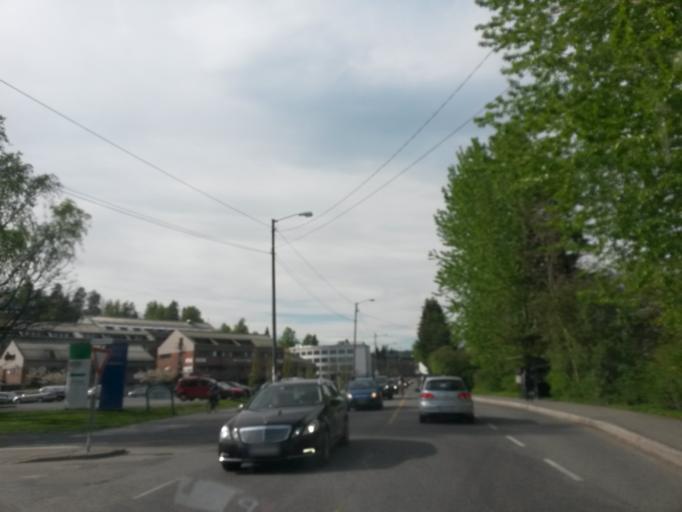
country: NO
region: Akershus
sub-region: Asker
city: Billingstad
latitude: 59.8629
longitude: 10.4906
